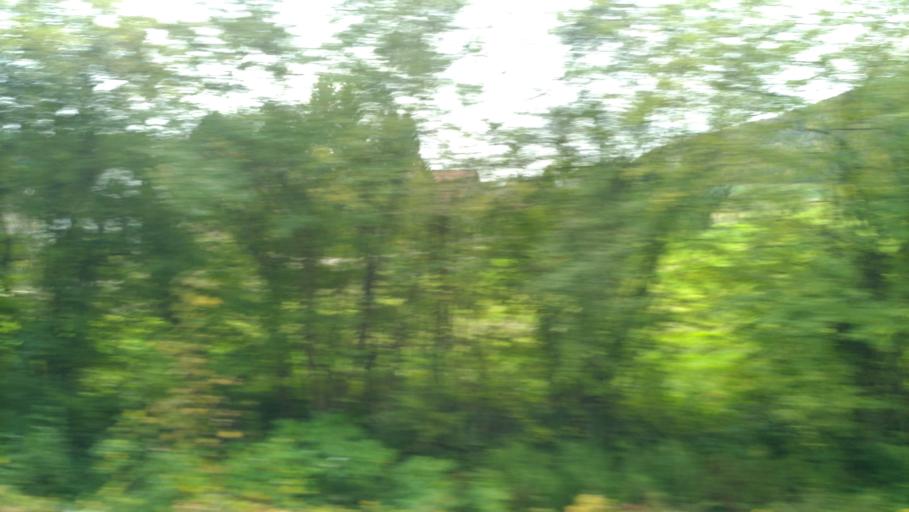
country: DE
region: Lower Saxony
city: Coppenbrugge
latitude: 52.1047
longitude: 9.5743
